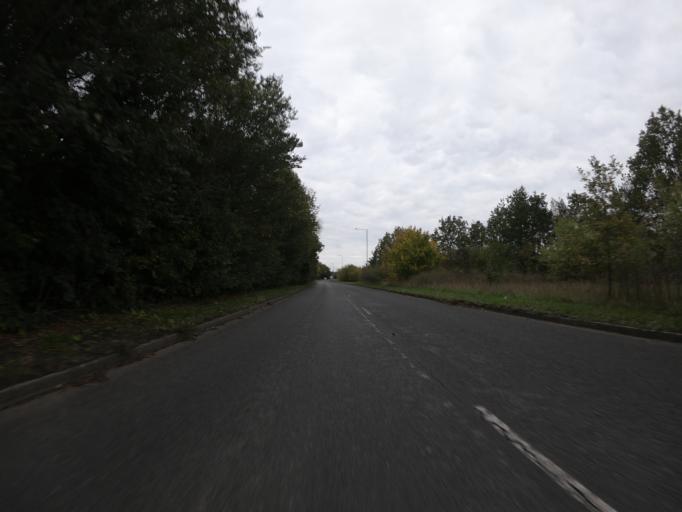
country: GB
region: England
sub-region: Borough of Thurrock
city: Chadwell St Mary
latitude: 51.4804
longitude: 0.3482
